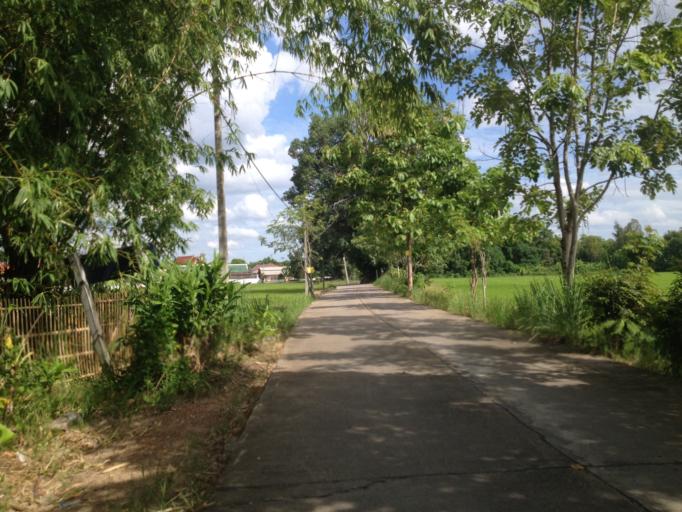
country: TH
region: Chiang Mai
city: Hang Dong
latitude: 18.7211
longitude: 98.9358
